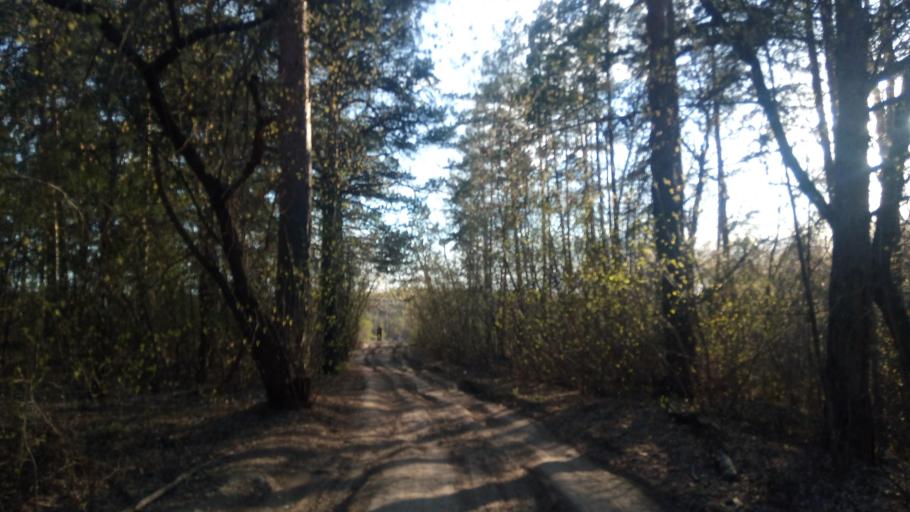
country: RU
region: Chelyabinsk
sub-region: Gorod Chelyabinsk
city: Chelyabinsk
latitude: 55.1488
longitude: 61.3292
